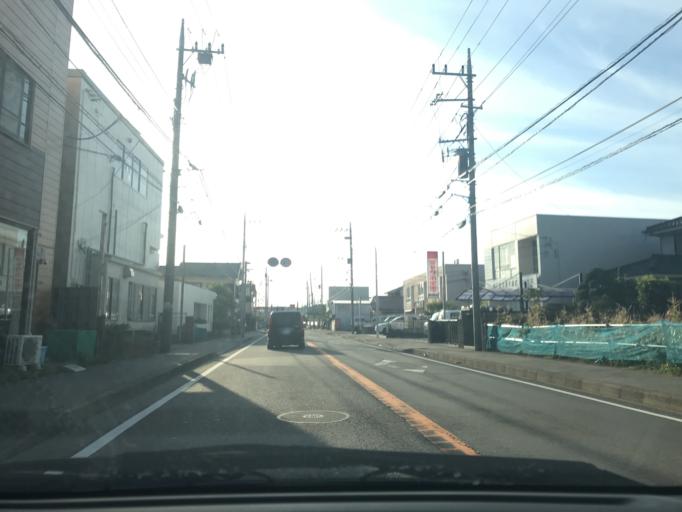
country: JP
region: Kanagawa
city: Fujisawa
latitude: 35.3421
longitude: 139.4726
